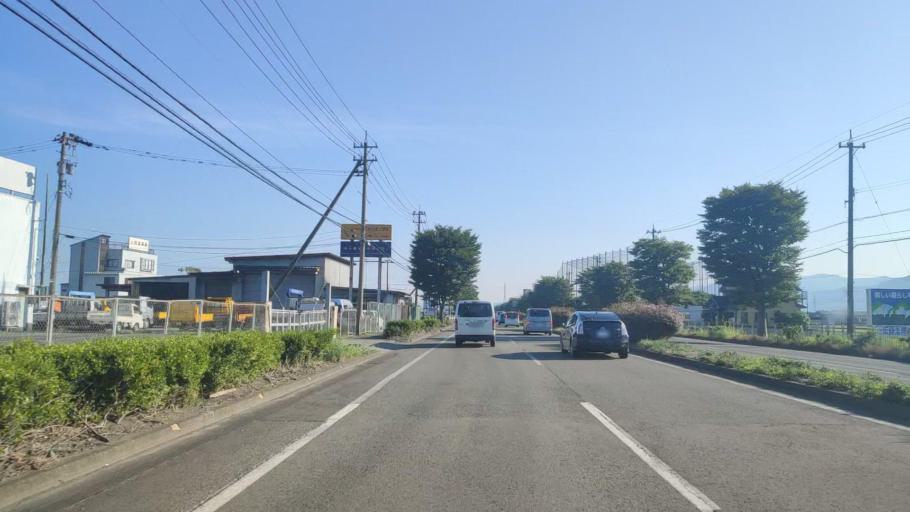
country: JP
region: Fukui
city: Maruoka
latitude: 36.1277
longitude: 136.2605
